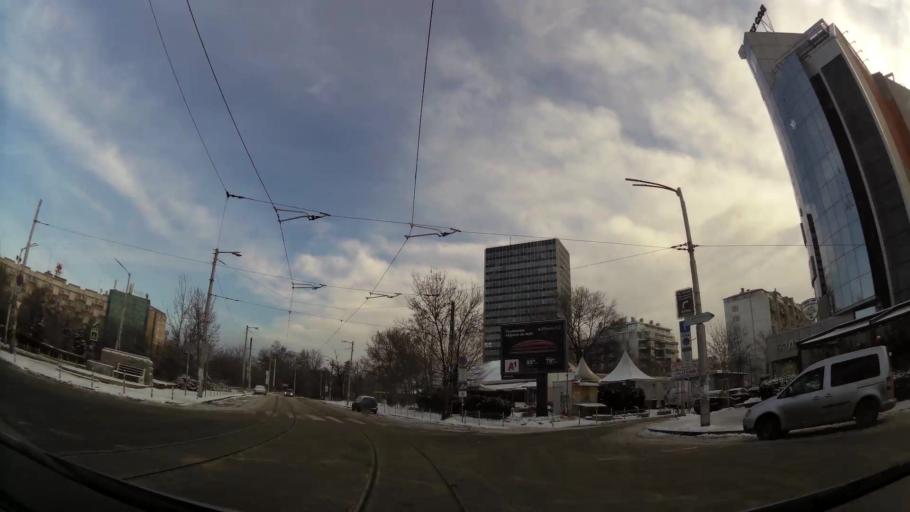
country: BG
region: Sofia-Capital
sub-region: Stolichna Obshtina
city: Sofia
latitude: 42.6714
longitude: 23.3212
